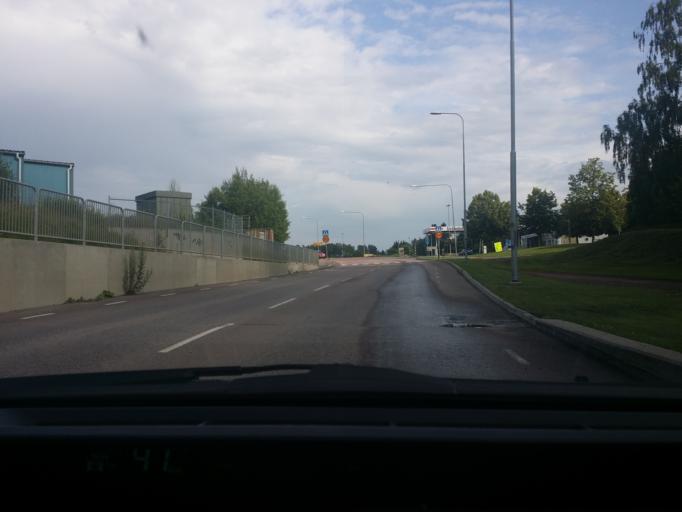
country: SE
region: Vaestmanland
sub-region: Hallstahammars Kommun
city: Kolback
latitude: 59.5653
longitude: 16.2379
